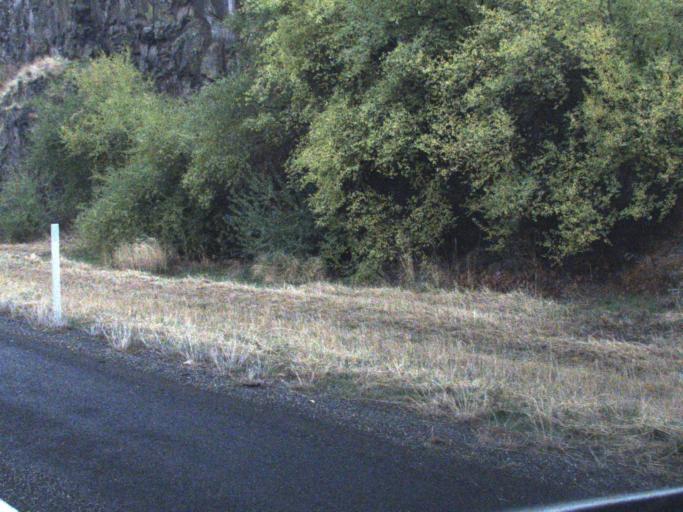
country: US
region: Washington
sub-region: Asotin County
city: Clarkston Heights-Vineland
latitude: 46.4263
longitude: -117.1339
